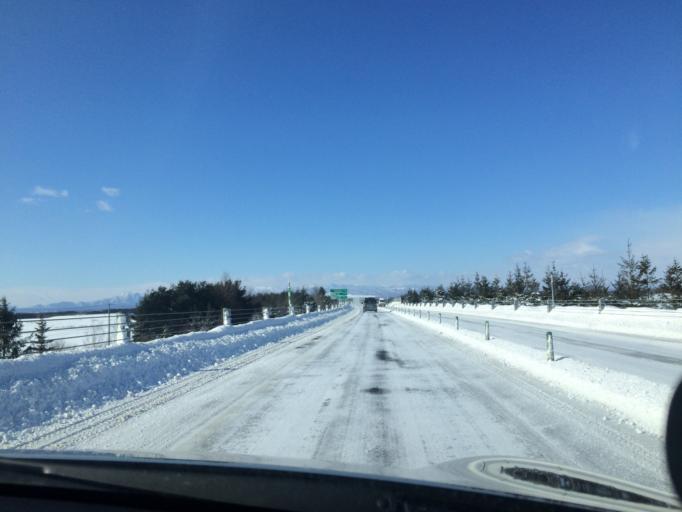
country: JP
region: Hokkaido
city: Chitose
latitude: 42.8839
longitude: 141.6947
